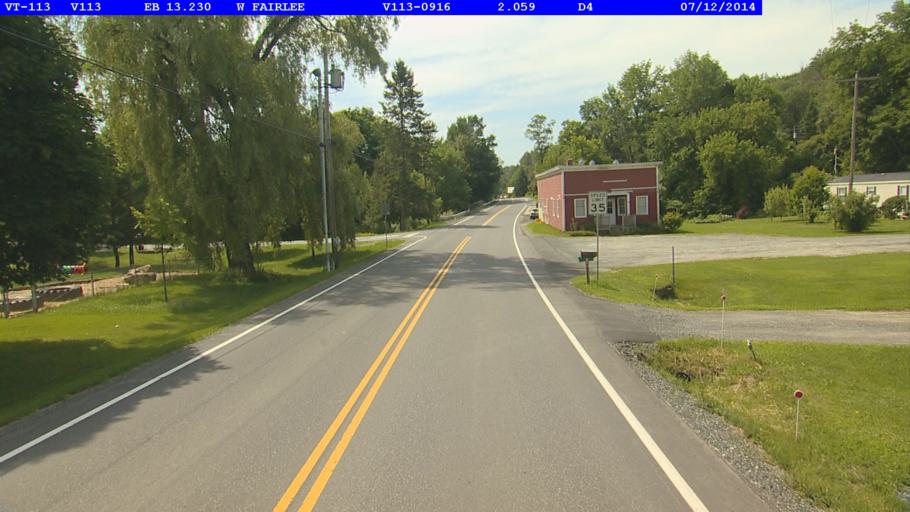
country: US
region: New Hampshire
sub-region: Grafton County
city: Orford
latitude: 43.9080
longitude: -72.2627
